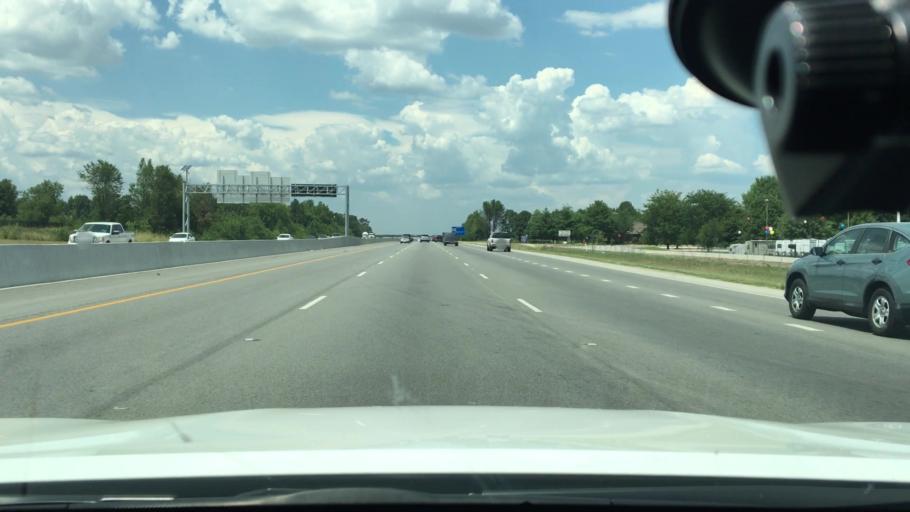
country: US
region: Arkansas
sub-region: Benton County
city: Lowell
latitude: 36.2586
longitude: -94.1503
